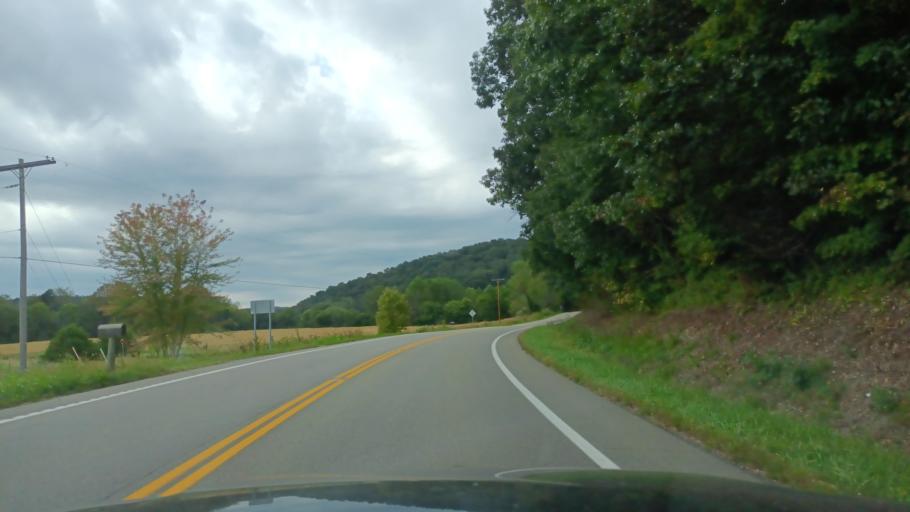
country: US
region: Ohio
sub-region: Vinton County
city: McArthur
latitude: 39.2701
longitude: -82.6401
